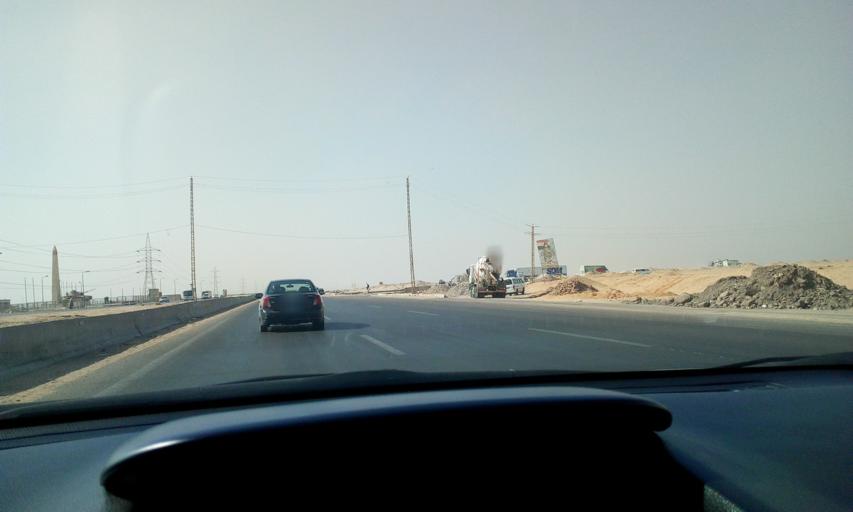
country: EG
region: Al Jizah
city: Madinat Sittah Uktubar
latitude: 29.8645
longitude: 31.0701
